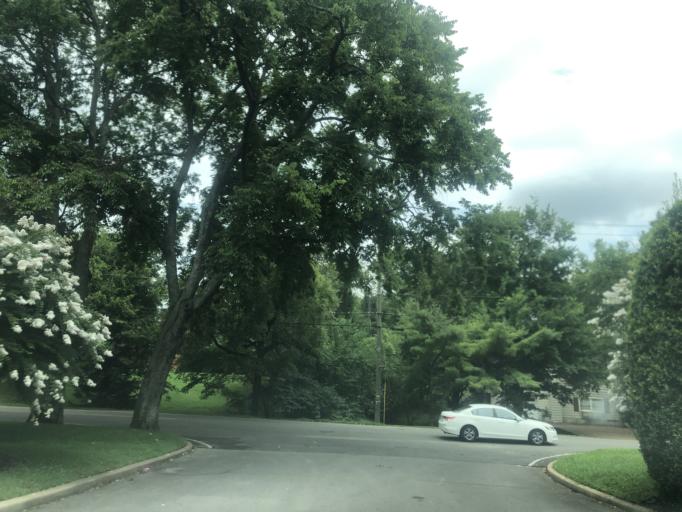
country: US
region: Tennessee
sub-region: Davidson County
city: Oak Hill
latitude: 36.0944
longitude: -86.7996
